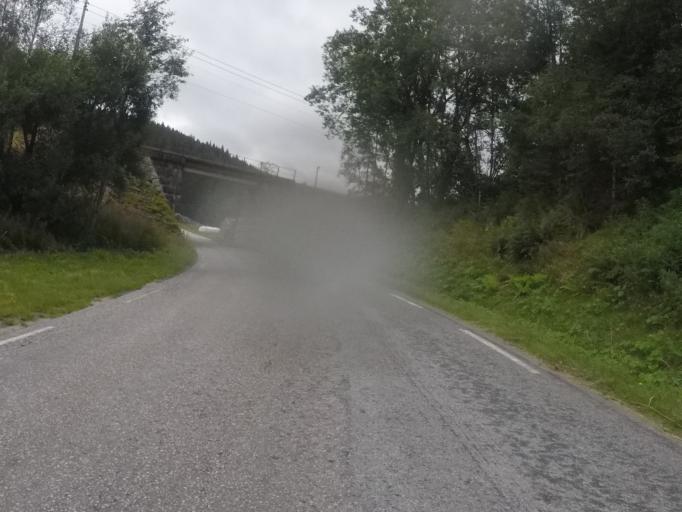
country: NO
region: Vest-Agder
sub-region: Audnedal
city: Konsmo
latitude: 58.2771
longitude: 7.3968
